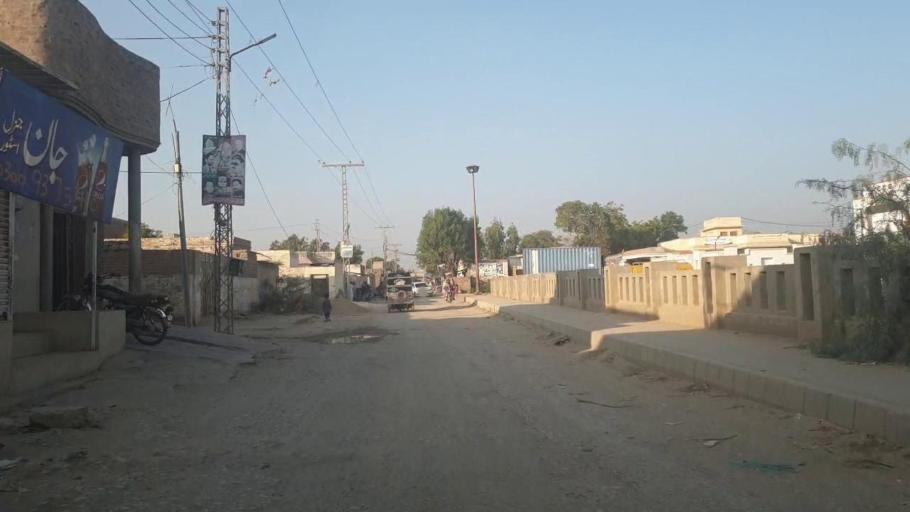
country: PK
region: Sindh
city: Jamshoro
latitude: 25.4383
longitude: 68.2905
